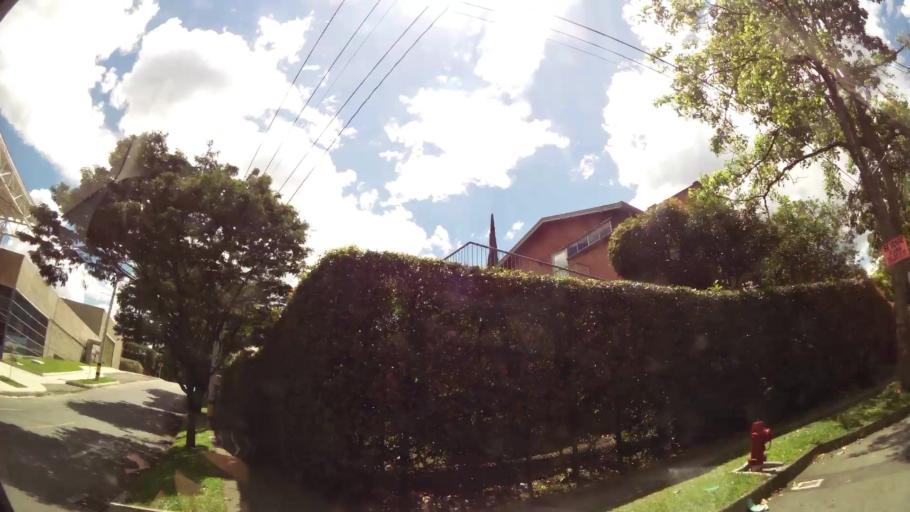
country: CO
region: Antioquia
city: Sabaneta
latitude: 6.1573
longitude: -75.6271
